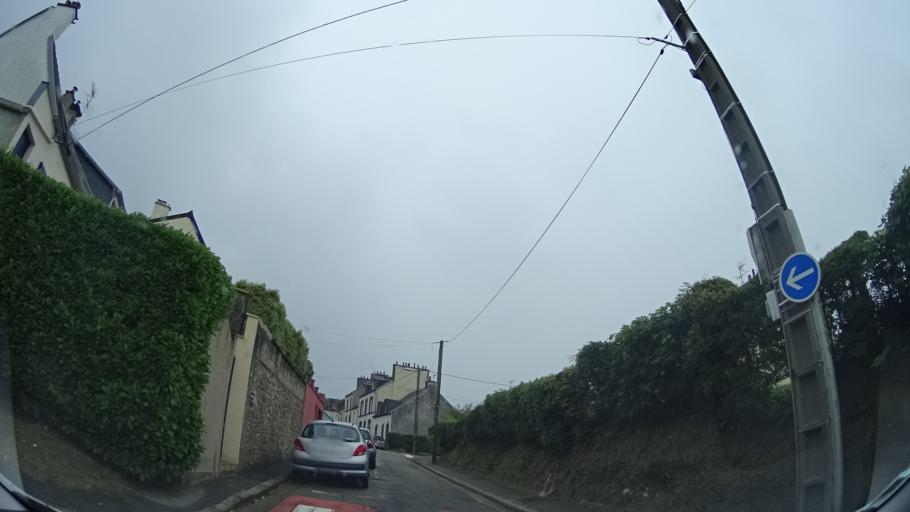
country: FR
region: Lower Normandy
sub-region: Departement de la Manche
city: Octeville
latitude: 49.6316
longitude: -1.6316
